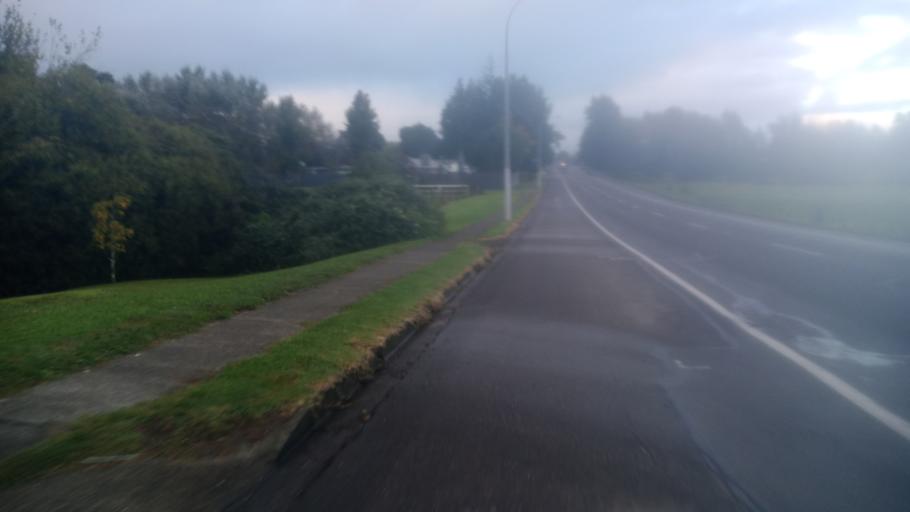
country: NZ
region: Gisborne
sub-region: Gisborne District
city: Gisborne
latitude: -38.6455
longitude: 178.0009
